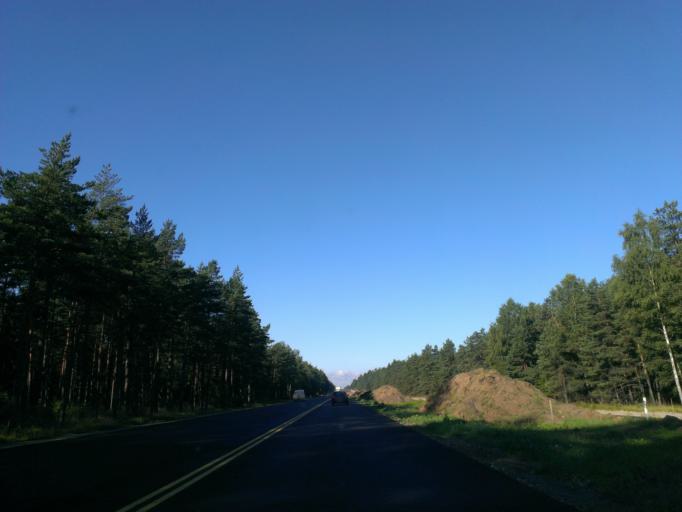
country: LV
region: Riga
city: Bergi
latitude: 57.0222
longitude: 24.3460
